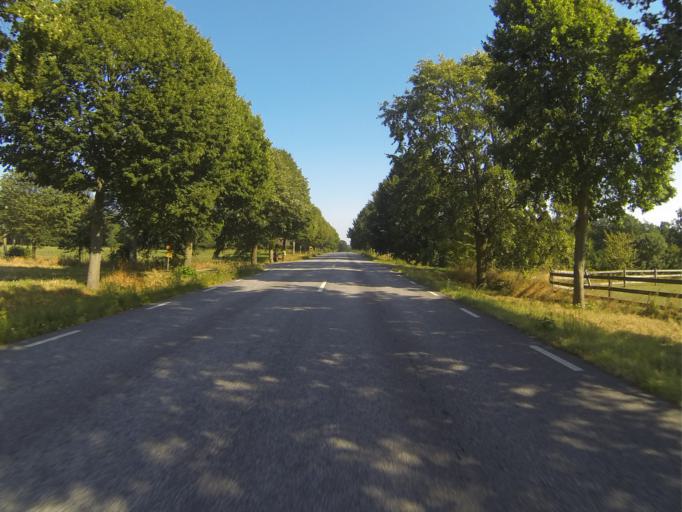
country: SE
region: Skane
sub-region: Hoors Kommun
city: Loberod
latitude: 55.7010
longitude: 13.5793
